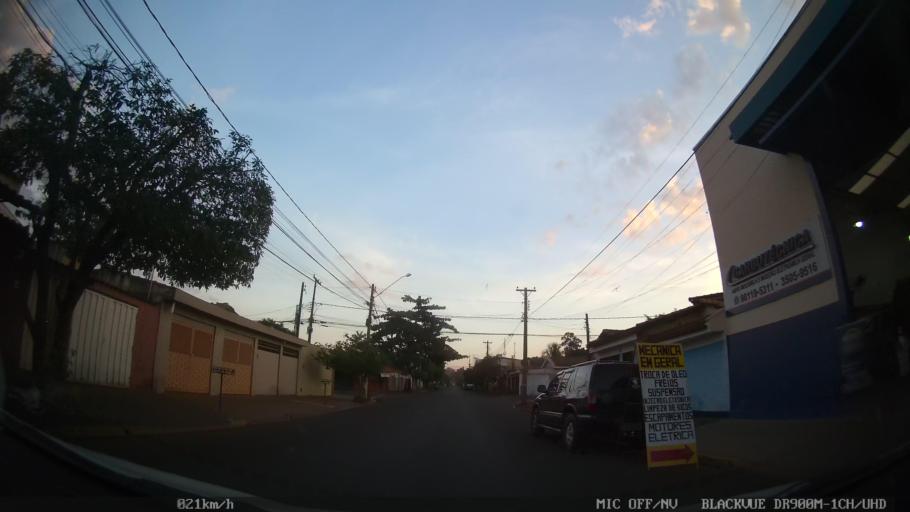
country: BR
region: Sao Paulo
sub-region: Ribeirao Preto
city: Ribeirao Preto
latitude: -21.1457
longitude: -47.8221
